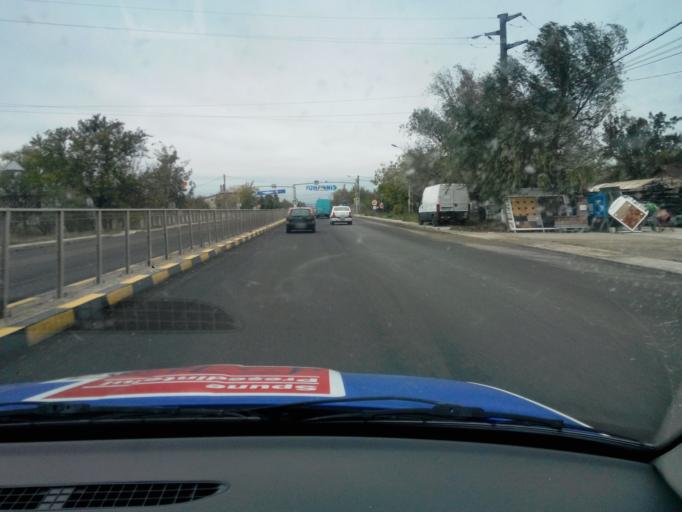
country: RO
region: Giurgiu
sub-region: Comuna Fratesti
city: Remus
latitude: 43.9350
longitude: 25.9769
